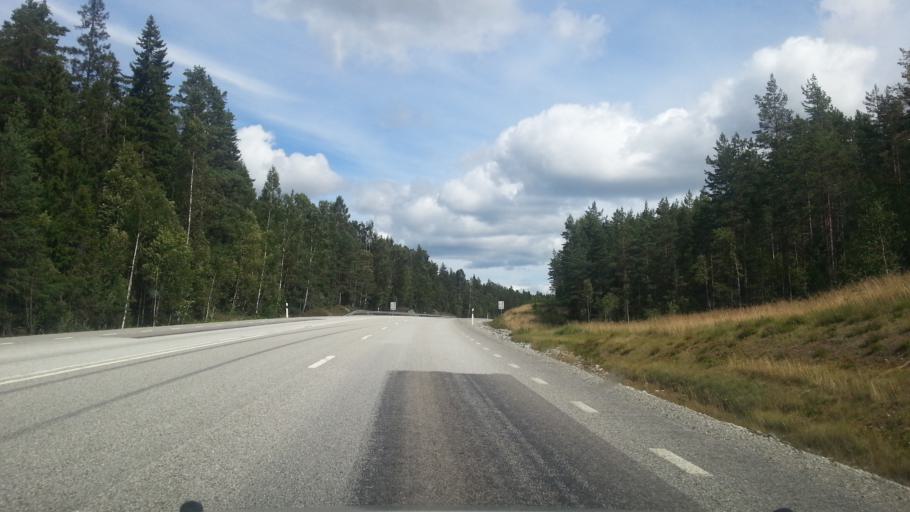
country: SE
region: Vaestmanland
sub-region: Skinnskattebergs Kommun
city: Skinnskatteberg
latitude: 59.8292
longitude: 15.5375
